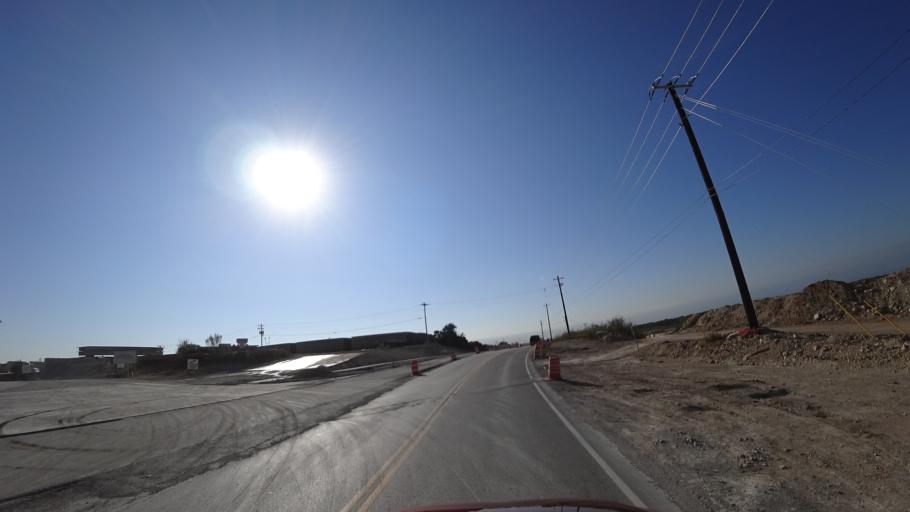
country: US
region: Texas
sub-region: Williamson County
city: Cedar Park
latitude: 30.5079
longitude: -97.8568
